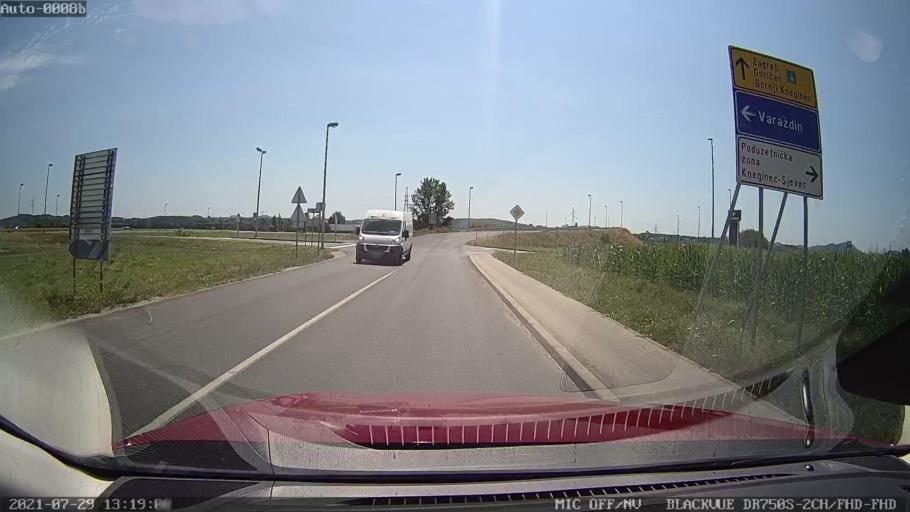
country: HR
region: Varazdinska
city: Varazdin
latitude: 46.2667
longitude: 16.3816
